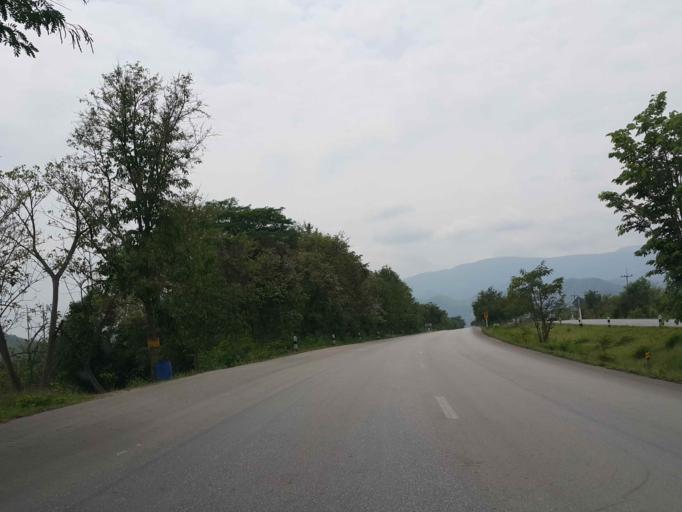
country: TH
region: Lampang
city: Sop Prap
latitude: 17.8623
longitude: 99.3284
